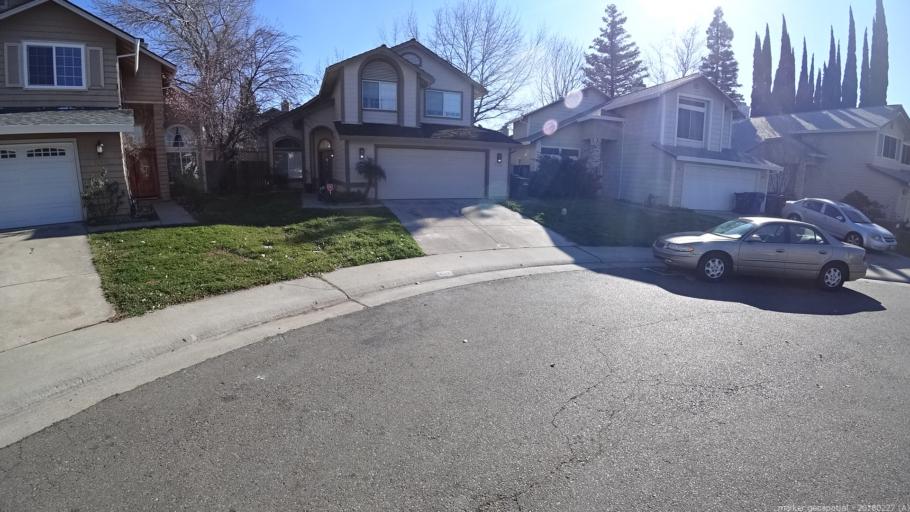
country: US
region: California
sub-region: Sacramento County
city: North Highlands
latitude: 38.7174
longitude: -121.3707
